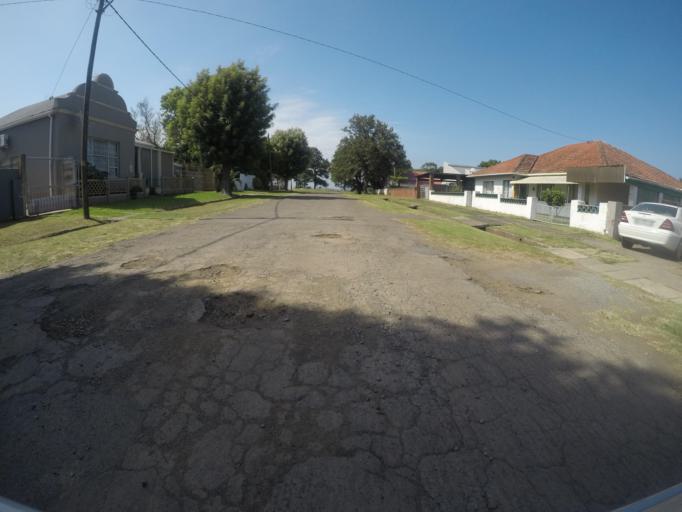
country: ZA
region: Eastern Cape
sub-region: Buffalo City Metropolitan Municipality
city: East London
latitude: -32.9692
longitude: 27.8779
